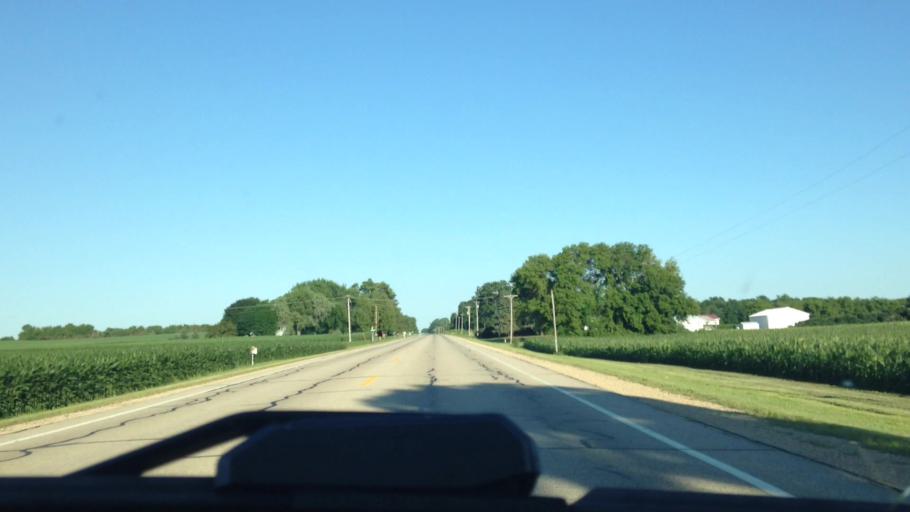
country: US
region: Wisconsin
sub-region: Dane County
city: De Forest
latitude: 43.3328
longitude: -89.2676
